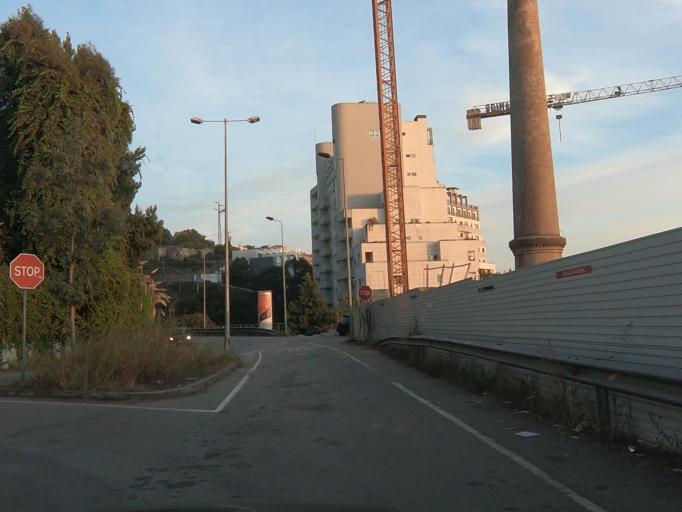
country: PT
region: Porto
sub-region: Gondomar
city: Valbom
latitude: 41.1418
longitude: -8.5732
